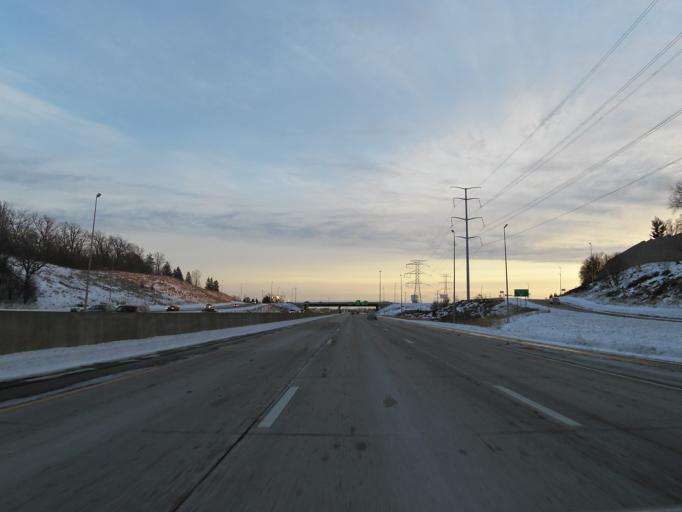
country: US
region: Minnesota
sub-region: Hennepin County
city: Eden Prairie
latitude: 44.8718
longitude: -93.4342
